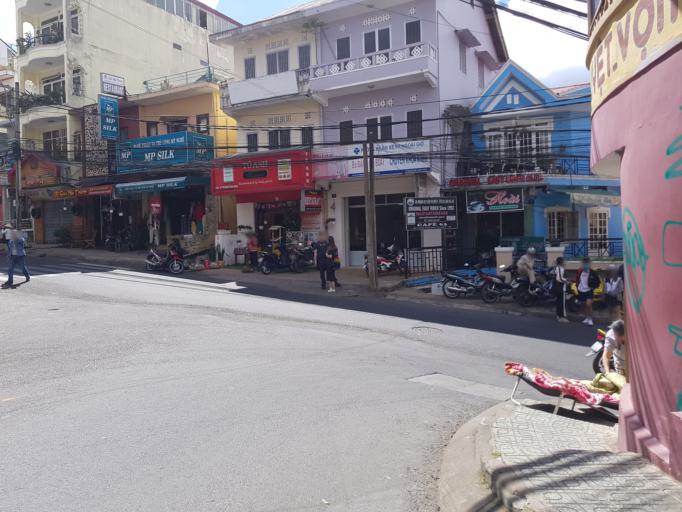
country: VN
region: Lam Dong
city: Da Lat
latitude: 11.9442
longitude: 108.4346
